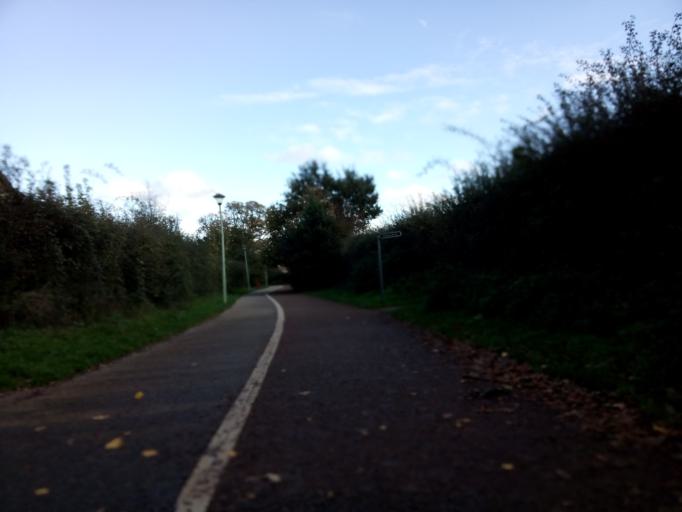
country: GB
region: England
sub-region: Suffolk
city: Kesgrave
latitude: 52.0621
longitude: 1.2469
